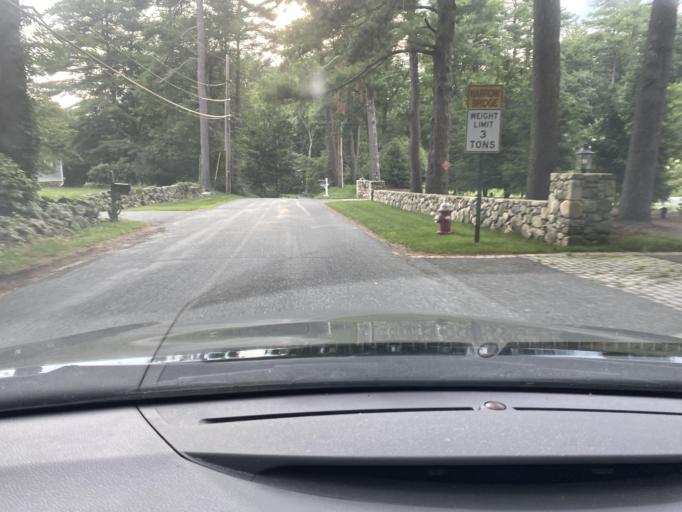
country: US
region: Massachusetts
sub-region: Norfolk County
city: Medfield
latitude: 42.1767
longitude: -71.2812
